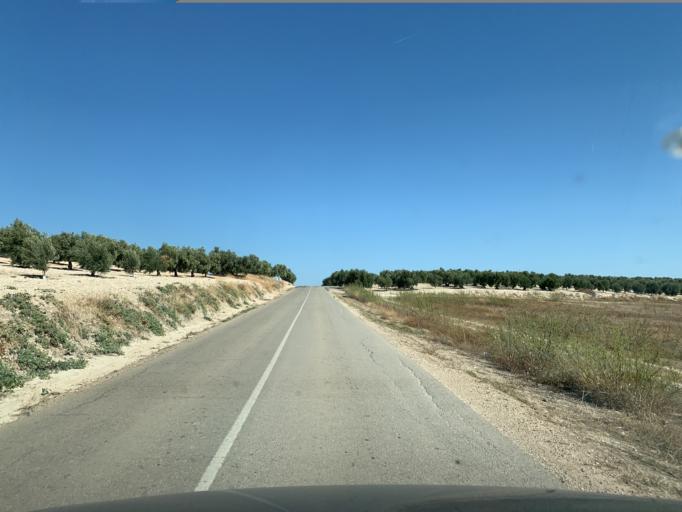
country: ES
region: Andalusia
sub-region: Provincia de Sevilla
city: El Rubio
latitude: 37.3447
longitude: -5.0213
